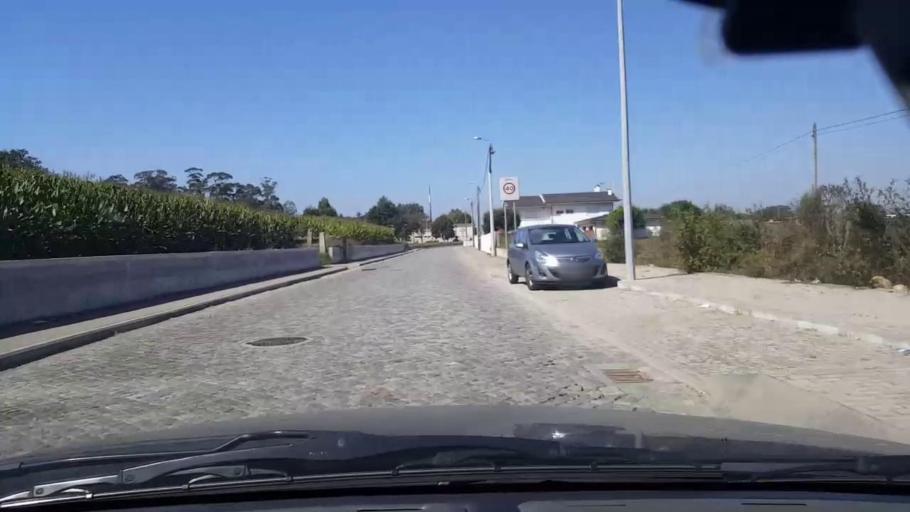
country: PT
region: Porto
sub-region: Vila do Conde
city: Arvore
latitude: 41.3065
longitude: -8.7172
